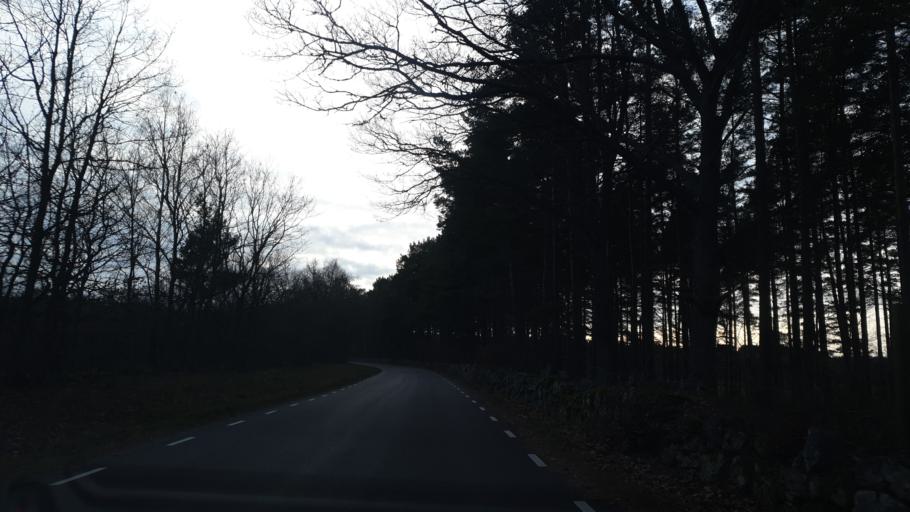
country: SE
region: Blekinge
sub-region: Karlskrona Kommun
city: Jaemjoe
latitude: 56.2224
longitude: 15.9861
